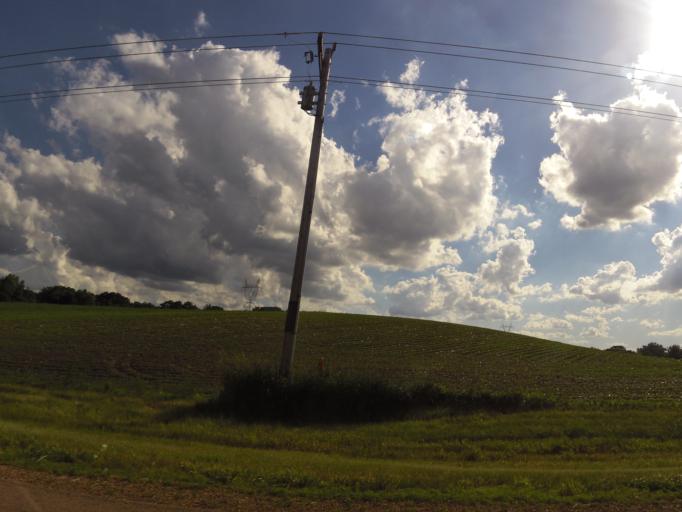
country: US
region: Minnesota
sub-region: Carver County
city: Victoria
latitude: 44.8147
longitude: -93.6842
